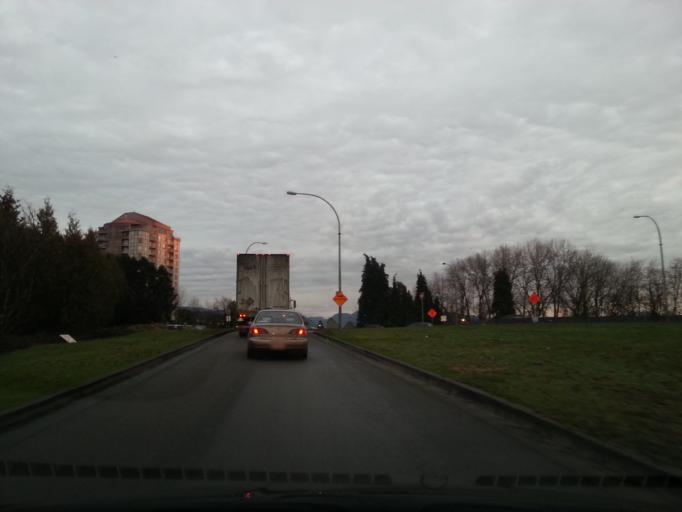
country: CA
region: British Columbia
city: New Westminster
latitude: 49.2090
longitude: -122.8996
